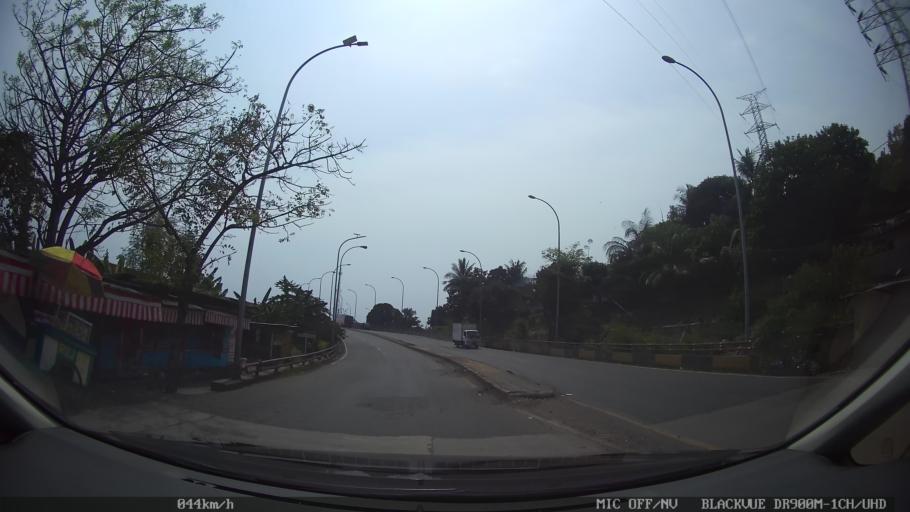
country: ID
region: Banten
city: Curug
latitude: -5.9396
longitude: 106.0040
